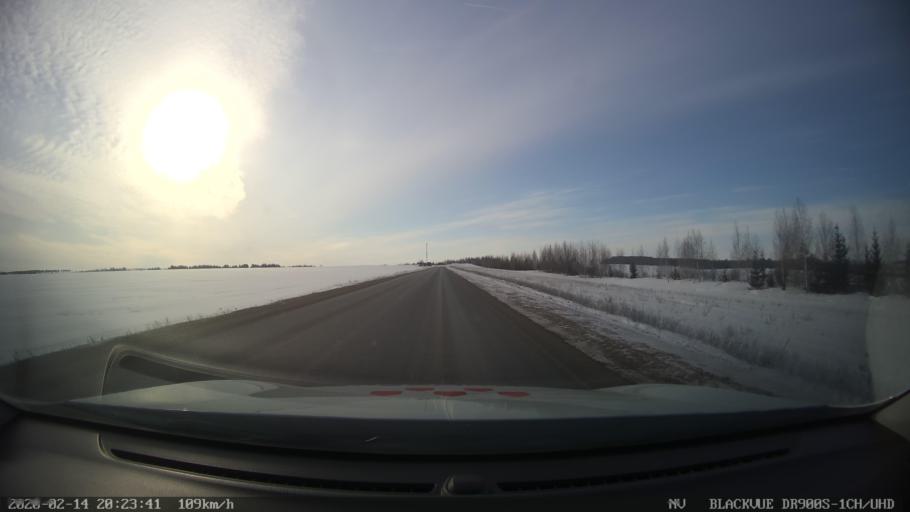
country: RU
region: Tatarstan
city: Verkhniy Uslon
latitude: 55.5241
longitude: 48.9695
